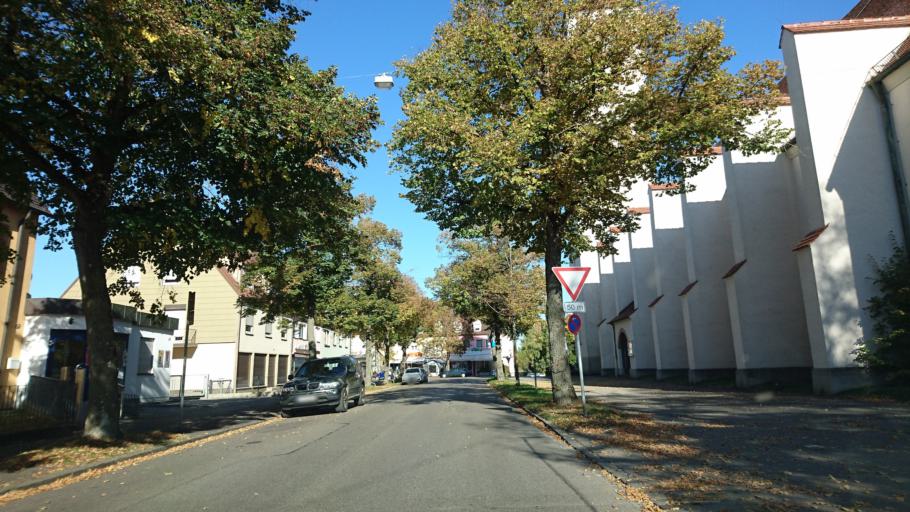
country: DE
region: Bavaria
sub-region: Swabia
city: Gersthofen
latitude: 48.3960
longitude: 10.8583
